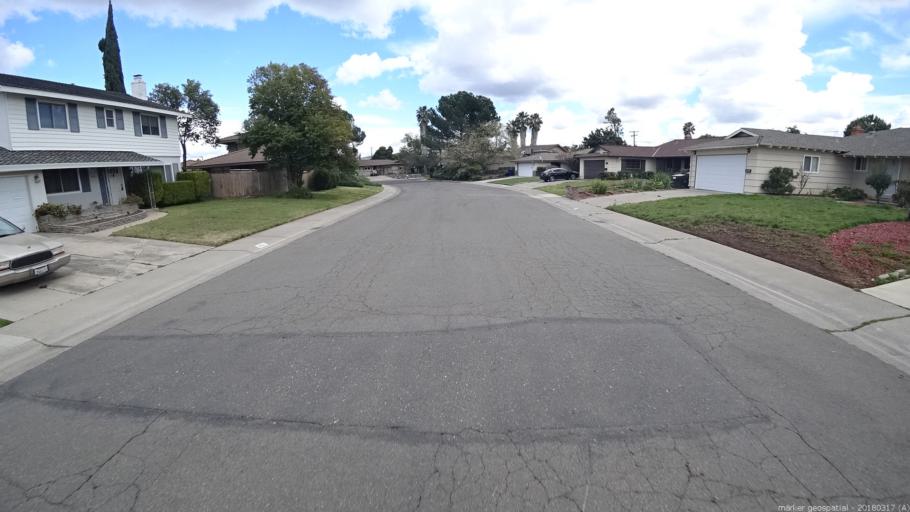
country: US
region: California
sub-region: Sacramento County
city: Parkway
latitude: 38.5023
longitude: -121.4544
